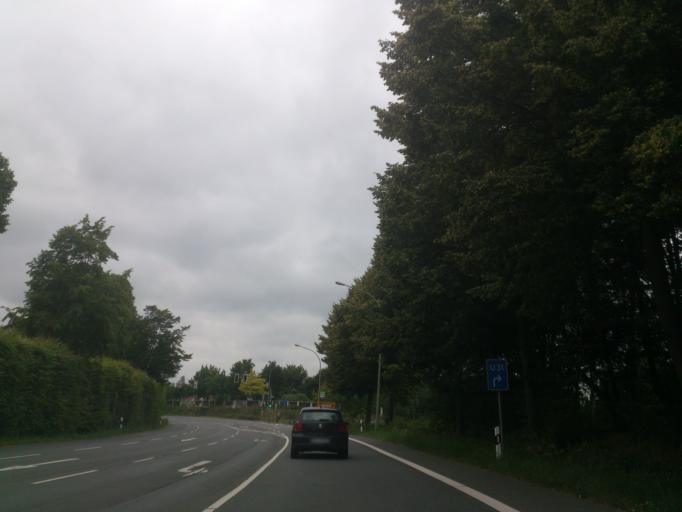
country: DE
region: North Rhine-Westphalia
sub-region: Regierungsbezirk Detmold
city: Paderborn
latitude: 51.7324
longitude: 8.7008
